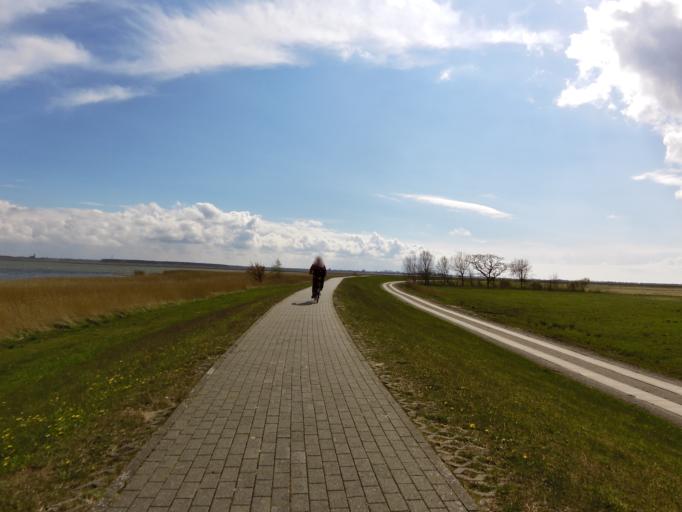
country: DE
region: Mecklenburg-Vorpommern
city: Zingst
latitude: 54.4311
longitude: 12.7171
